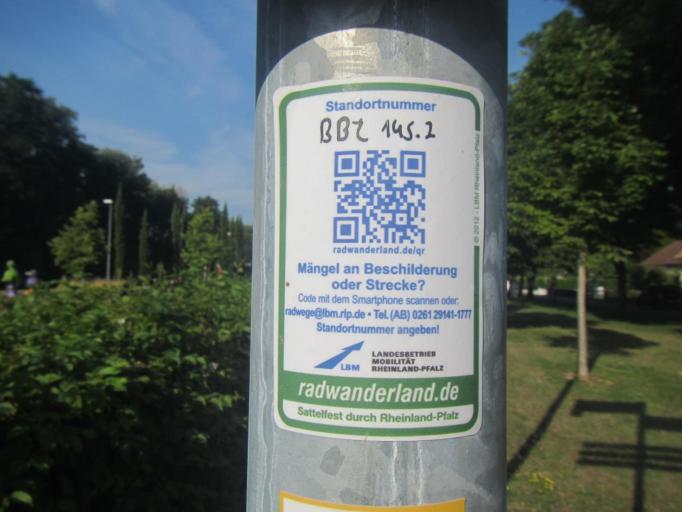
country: DE
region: Rheinland-Pfalz
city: Kapsweyer
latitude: 49.0392
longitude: 8.0226
